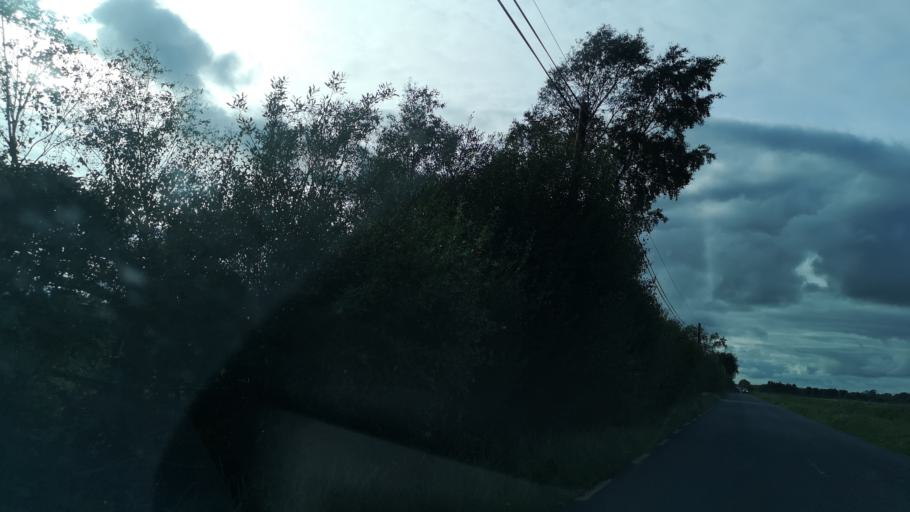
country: IE
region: Leinster
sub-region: Uibh Fhaili
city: Banagher
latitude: 53.2816
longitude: -8.0683
